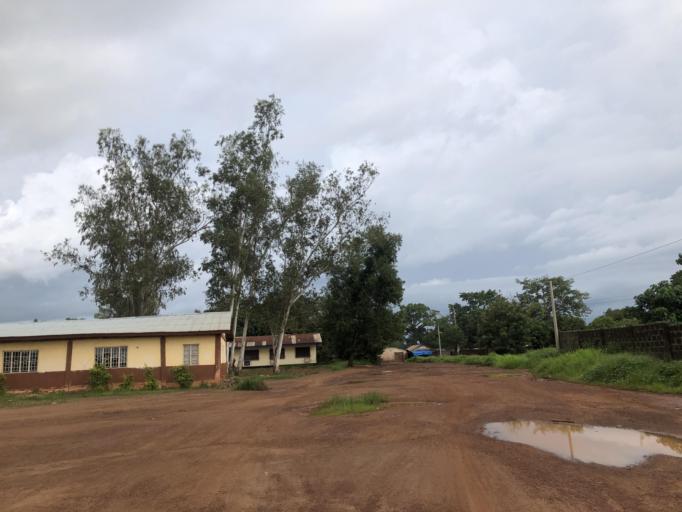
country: SL
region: Northern Province
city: Port Loko
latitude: 8.7669
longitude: -12.7815
